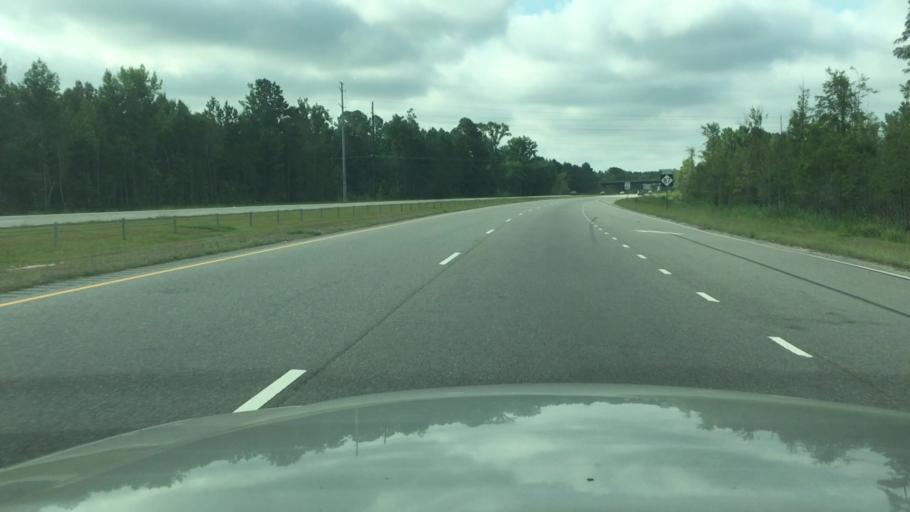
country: US
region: North Carolina
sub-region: Cumberland County
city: Fayetteville
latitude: 35.0285
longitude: -78.8737
